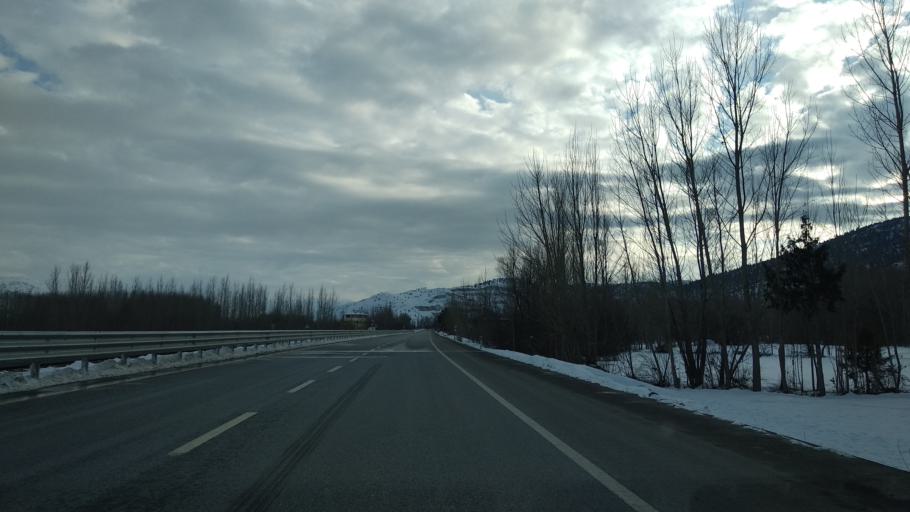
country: TR
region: Kahramanmaras
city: Goksun
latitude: 38.0490
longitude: 36.4684
